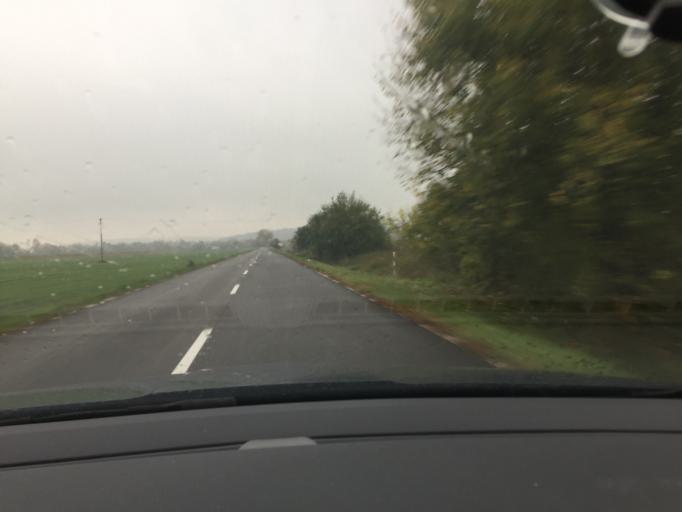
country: SK
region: Nitriansky
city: Zeliezovce
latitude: 47.9878
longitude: 18.7672
